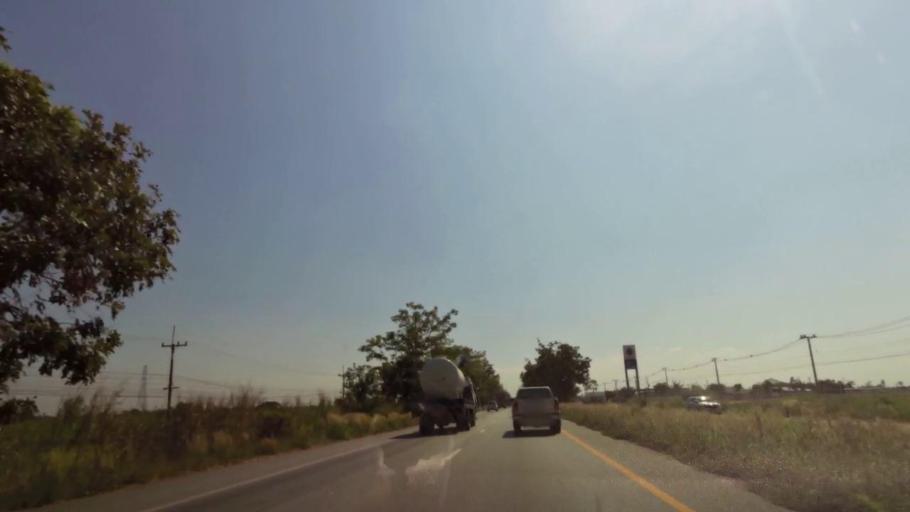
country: TH
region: Nakhon Sawan
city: Kao Liao
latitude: 15.8346
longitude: 100.1179
